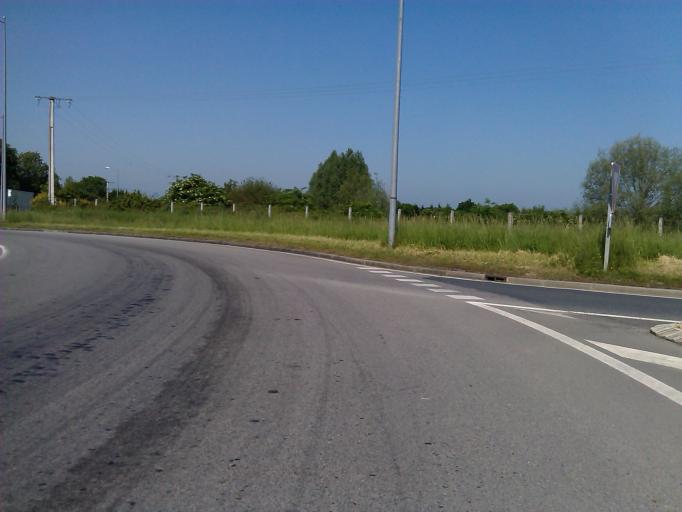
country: FR
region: Centre
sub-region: Departement de l'Indre
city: Neuvy-Saint-Sepulchre
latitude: 46.5989
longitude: 1.7745
